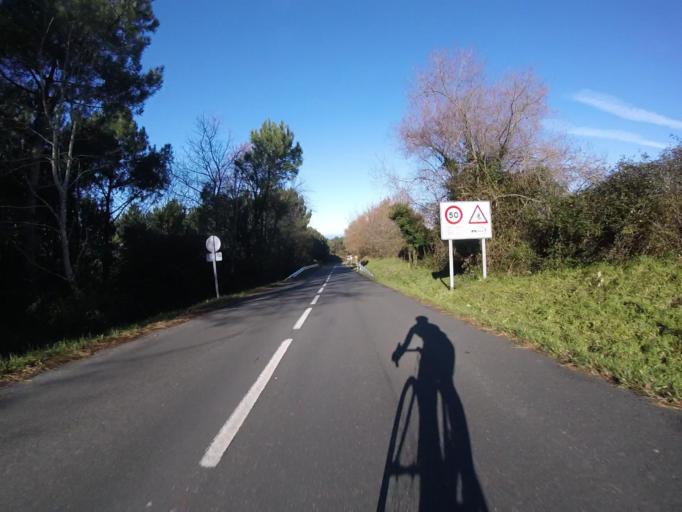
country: ES
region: Basque Country
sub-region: Provincia de Guipuzcoa
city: Fuenterrabia
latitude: 43.3685
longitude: -1.8320
